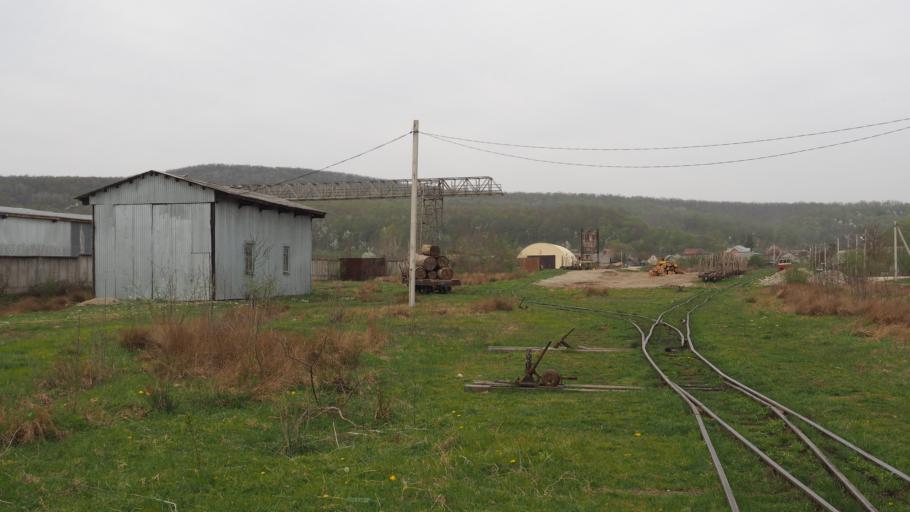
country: RU
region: Krasnodarskiy
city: Neftegorsk
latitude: 44.2468
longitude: 39.7648
